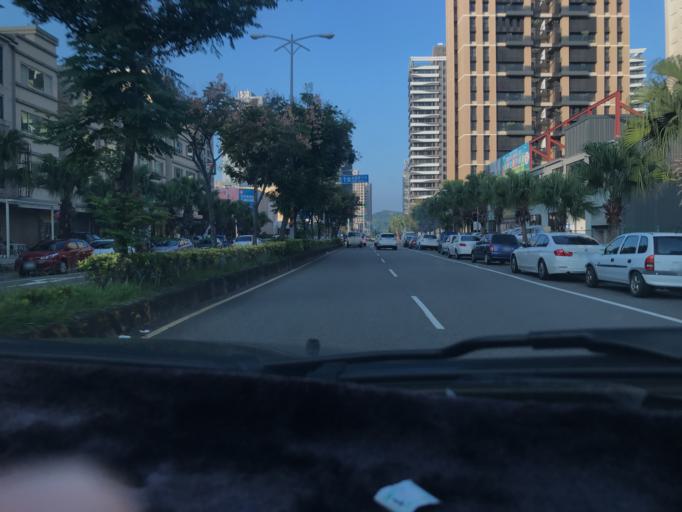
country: TW
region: Taiwan
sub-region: Hsinchu
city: Zhubei
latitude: 24.8075
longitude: 121.0322
